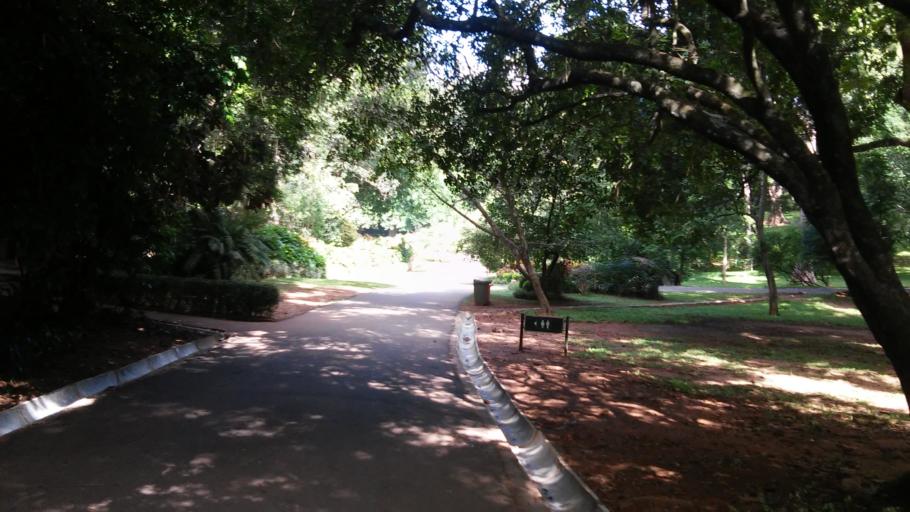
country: LK
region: Central
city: Kandy
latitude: 7.2681
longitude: 80.5957
